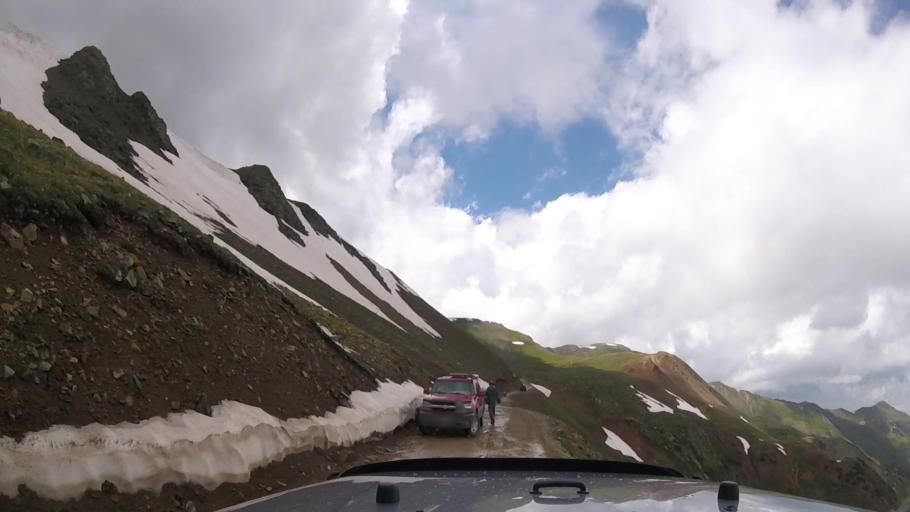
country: US
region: Colorado
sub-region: Ouray County
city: Ouray
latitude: 37.9194
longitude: -107.6237
